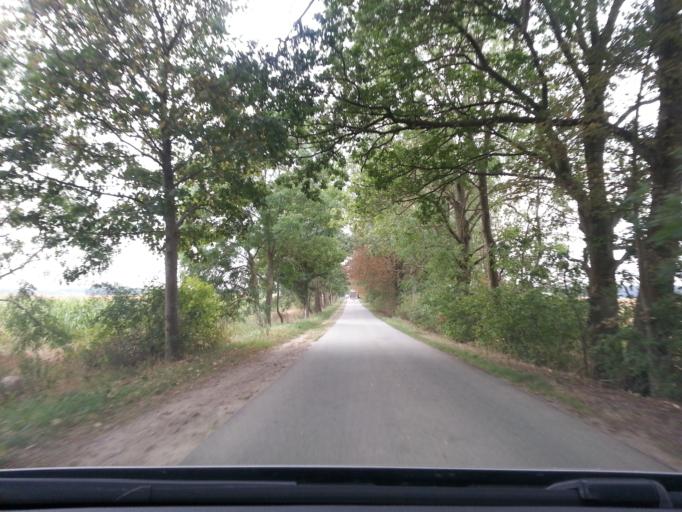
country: DE
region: Mecklenburg-Vorpommern
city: Ferdinandshof
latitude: 53.6700
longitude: 13.9162
